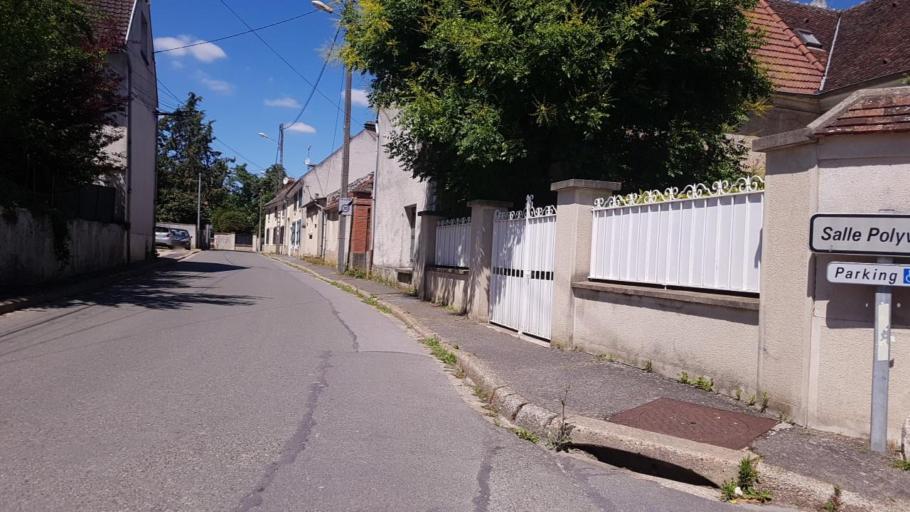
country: FR
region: Ile-de-France
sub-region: Departement de Seine-et-Marne
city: Sammeron
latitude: 48.9543
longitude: 3.0703
